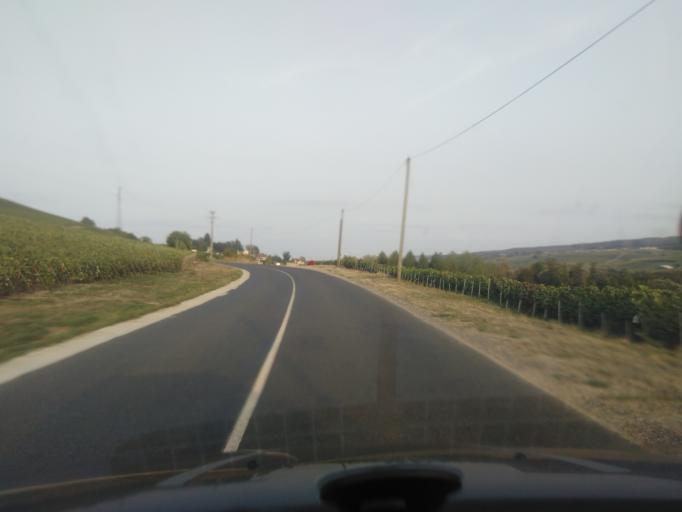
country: FR
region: Champagne-Ardenne
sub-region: Departement de la Marne
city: Mareuil-le-Port
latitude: 49.0808
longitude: 3.8066
